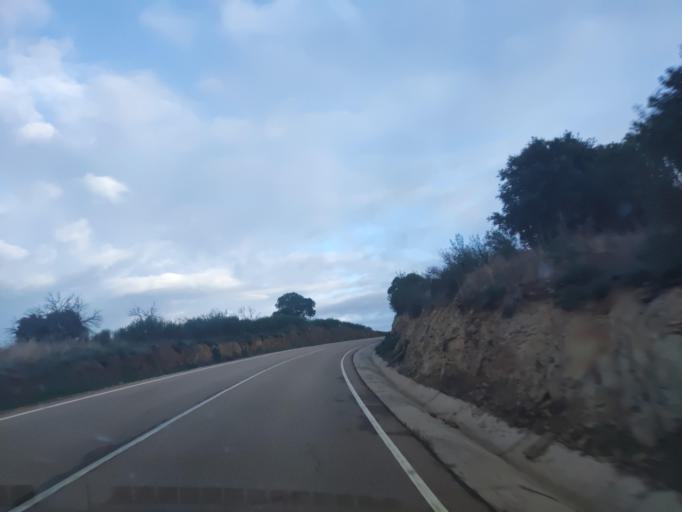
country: ES
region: Castille and Leon
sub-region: Provincia de Salamanca
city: Castillejo de Martin Viejo
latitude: 40.7141
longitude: -6.6439
